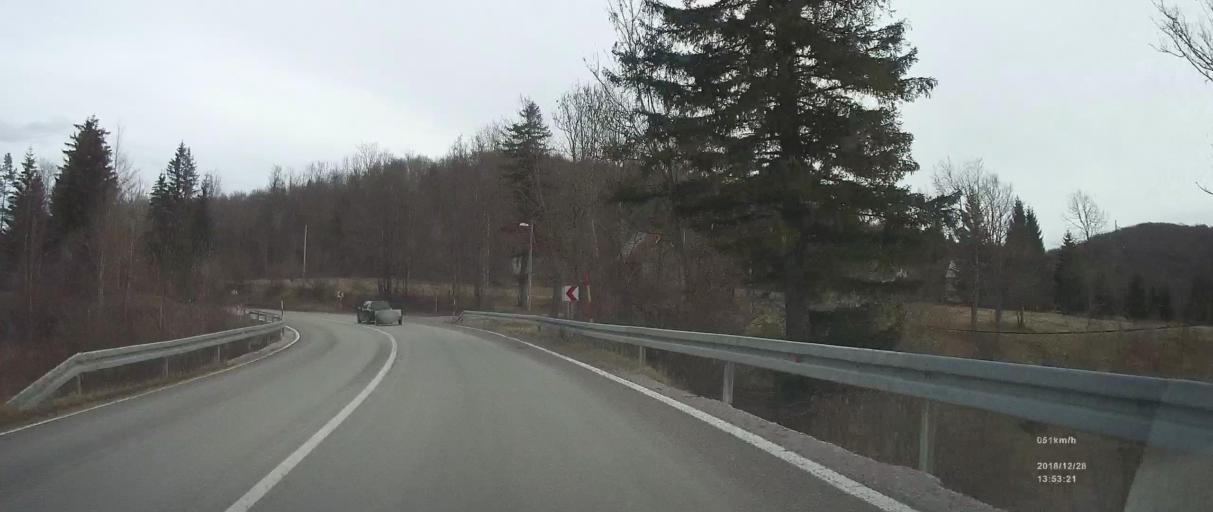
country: HR
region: Primorsko-Goranska
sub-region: Grad Delnice
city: Delnice
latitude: 45.3853
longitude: 14.8517
